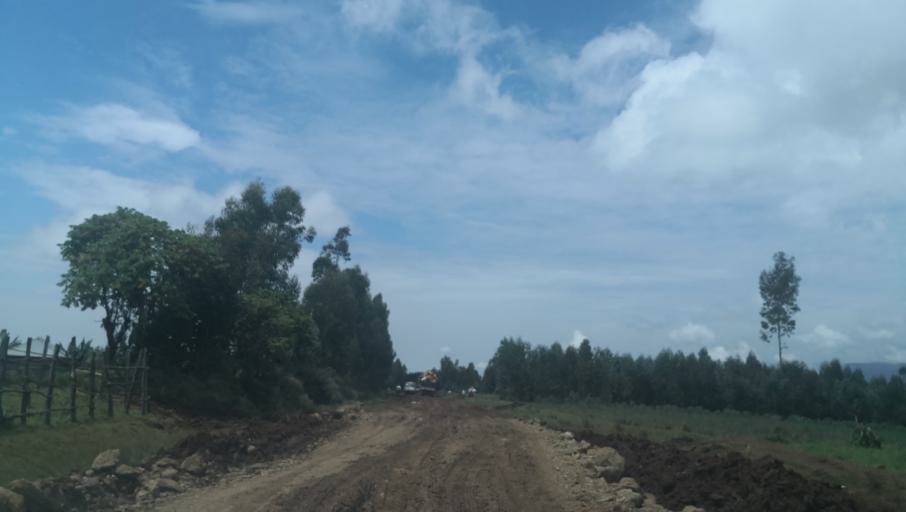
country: ET
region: Southern Nations, Nationalities, and People's Region
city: Butajira
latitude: 8.2925
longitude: 38.4741
